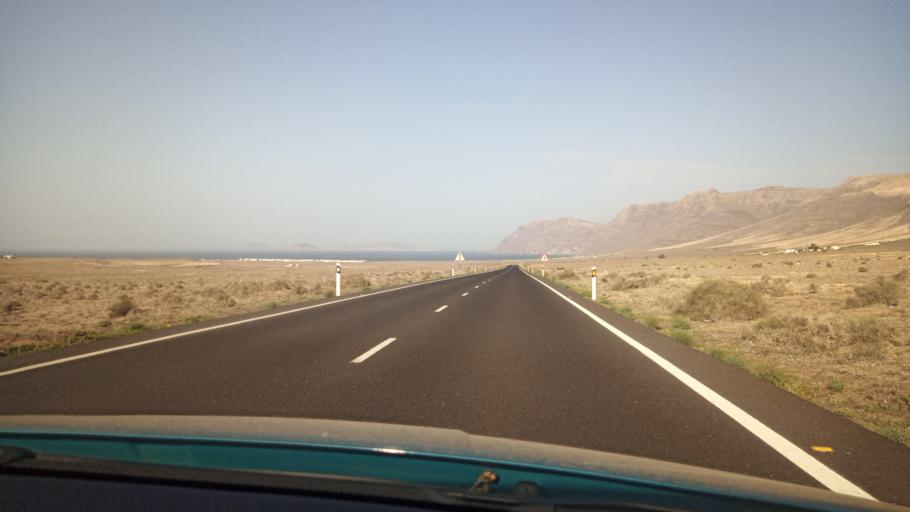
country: ES
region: Canary Islands
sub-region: Provincia de Las Palmas
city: Teguise
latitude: 29.0798
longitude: -13.5756
